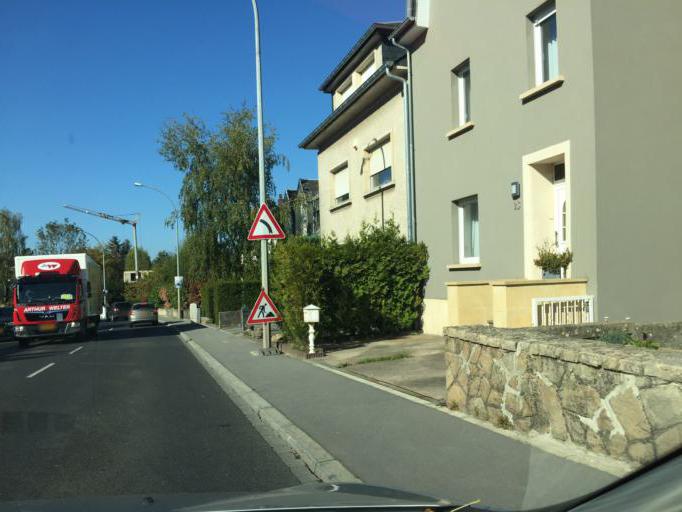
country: LU
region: Luxembourg
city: Bridel
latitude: 49.6593
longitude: 6.0814
